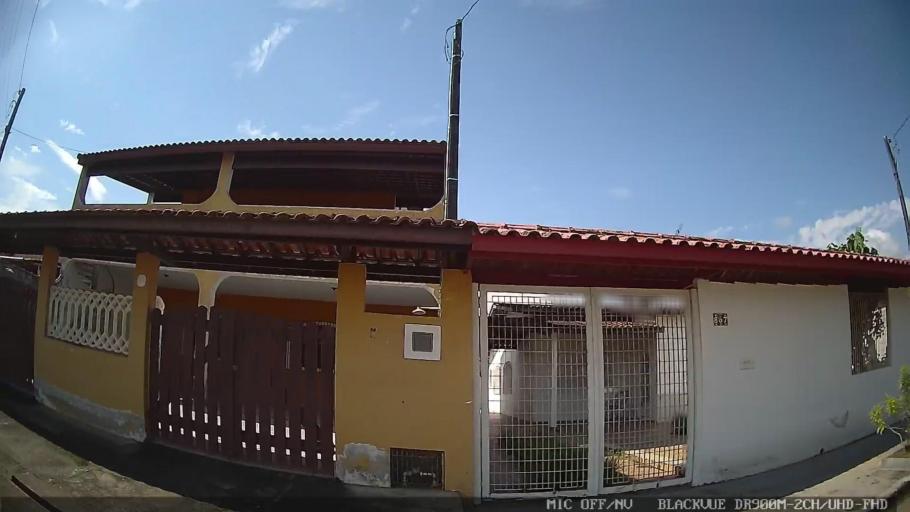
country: BR
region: Sao Paulo
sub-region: Caraguatatuba
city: Caraguatatuba
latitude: -23.6700
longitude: -45.4452
